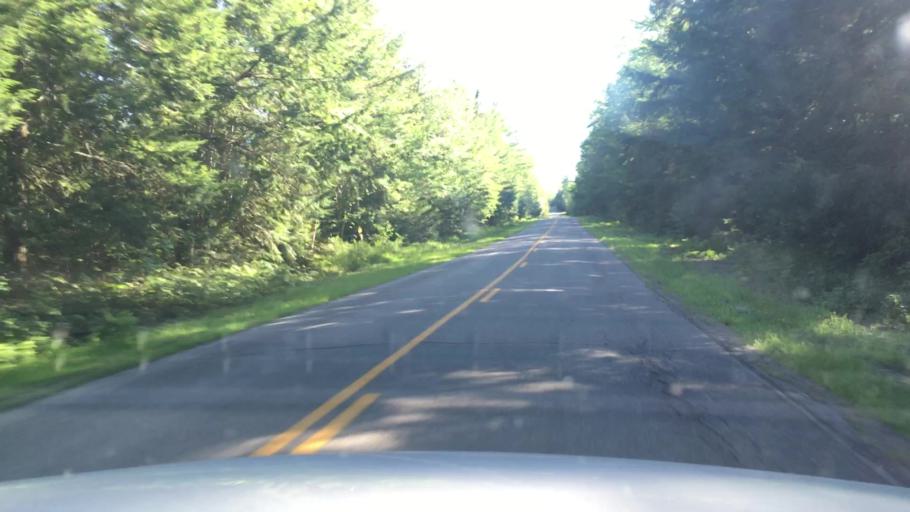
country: US
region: Maine
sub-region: Penobscot County
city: Enfield
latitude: 45.2199
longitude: -68.5815
